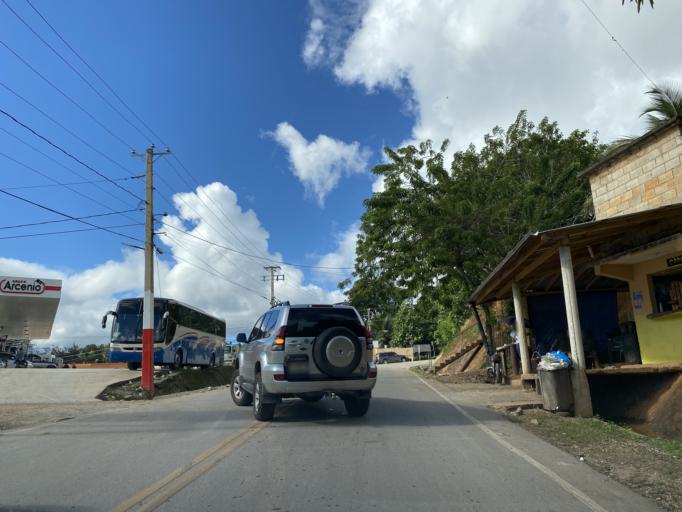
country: DO
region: Samana
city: Samana
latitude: 19.2131
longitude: -69.3551
